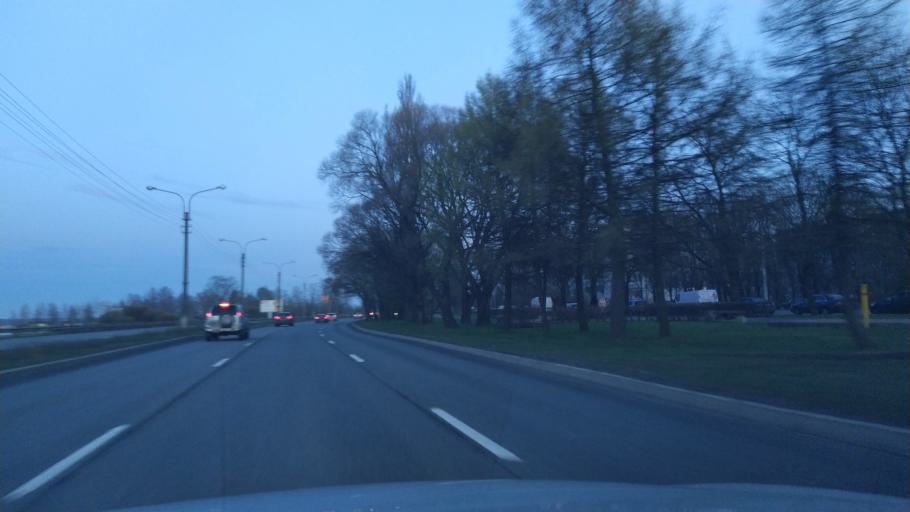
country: RU
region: St.-Petersburg
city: Sestroretsk
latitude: 60.1026
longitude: 29.9783
